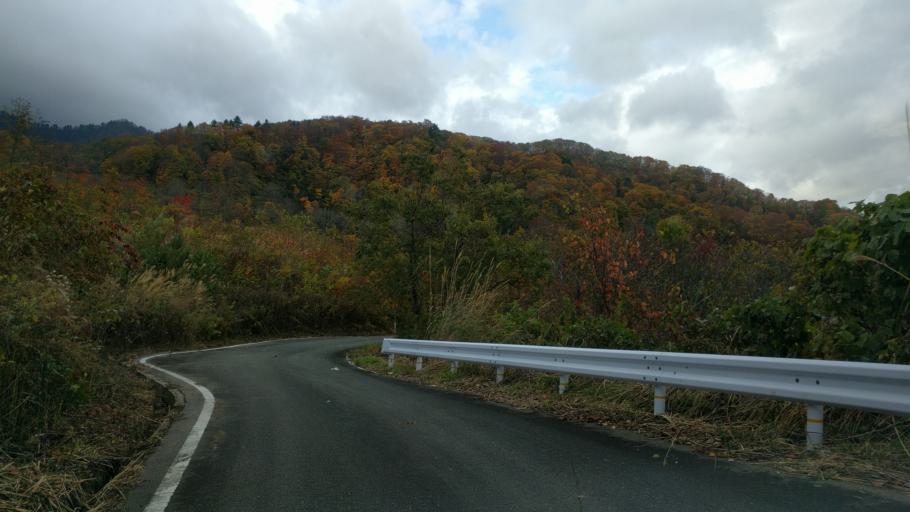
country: JP
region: Fukushima
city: Kitakata
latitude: 37.3904
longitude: 139.7199
